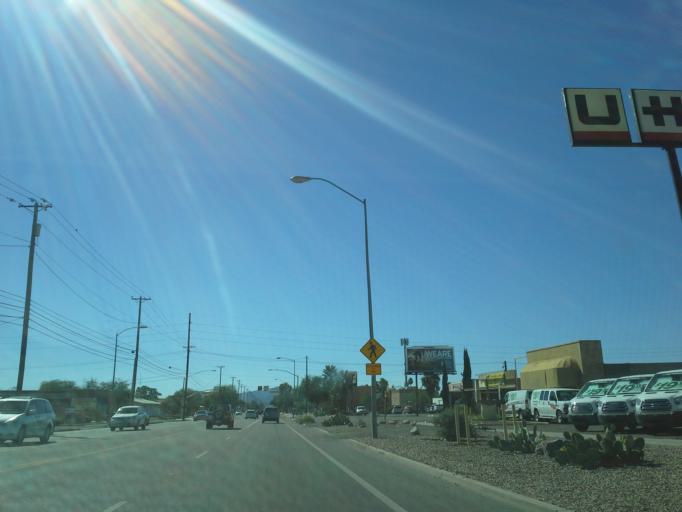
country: US
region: Arizona
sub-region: Pima County
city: Tucson
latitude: 32.2506
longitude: -110.9166
